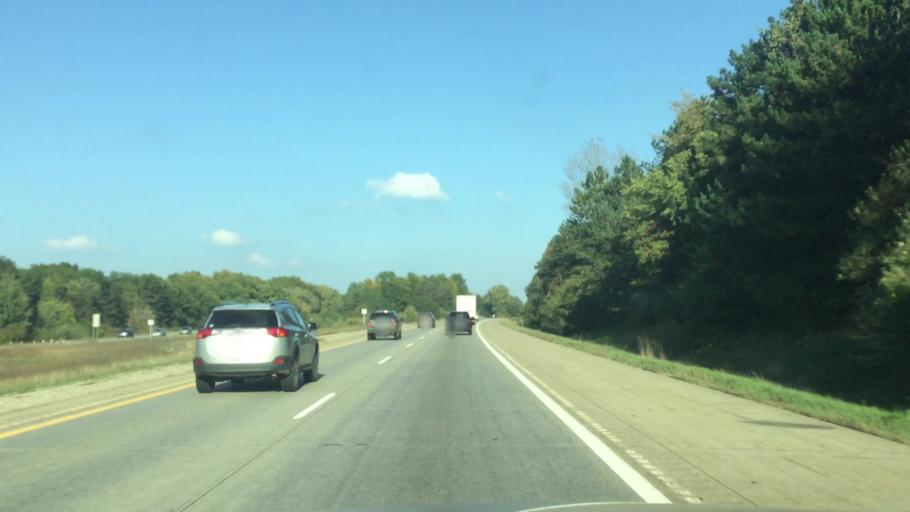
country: US
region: Michigan
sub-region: Jackson County
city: Grass Lake
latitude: 42.2884
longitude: -84.2741
